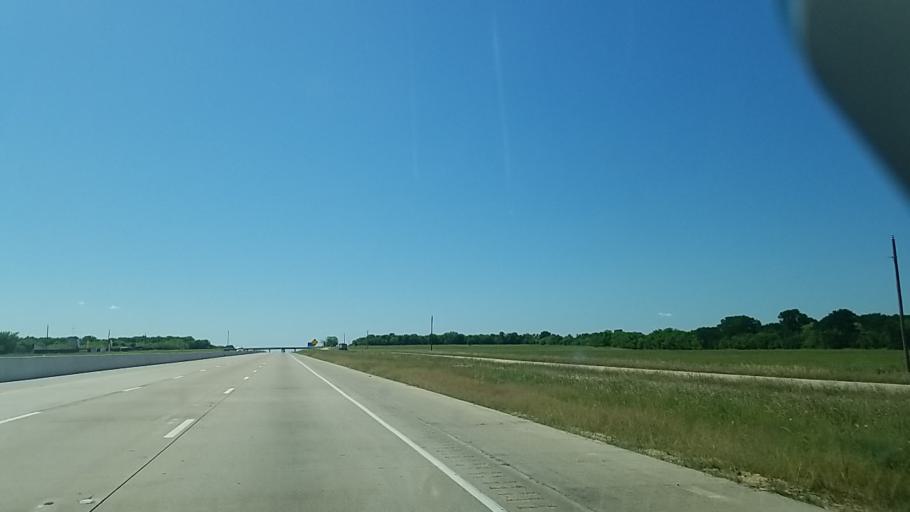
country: US
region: Texas
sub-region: Freestone County
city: Wortham
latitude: 31.9011
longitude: -96.3765
